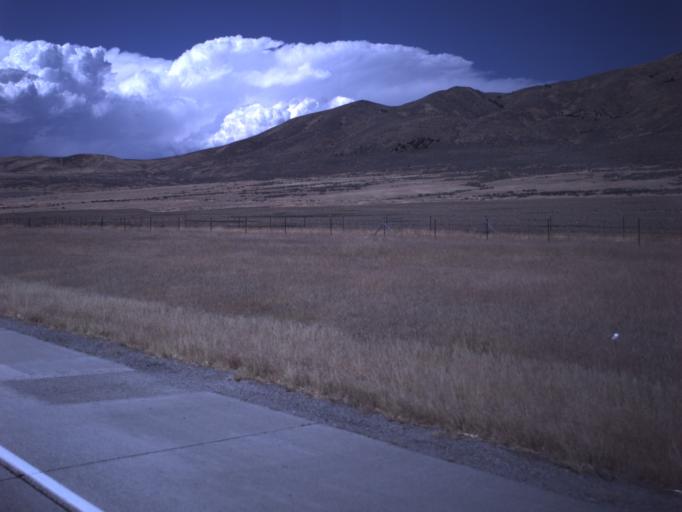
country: US
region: Utah
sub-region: Box Elder County
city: Garland
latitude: 41.7620
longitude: -112.2632
